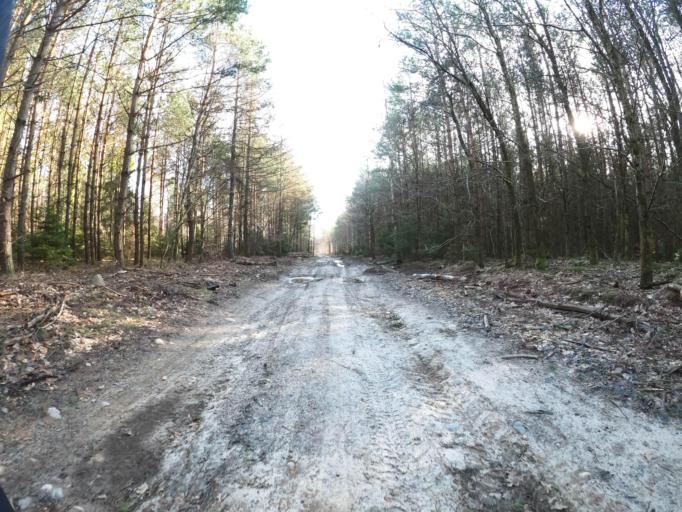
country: PL
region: West Pomeranian Voivodeship
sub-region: Powiat koszalinski
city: Polanow
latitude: 54.2113
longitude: 16.6461
